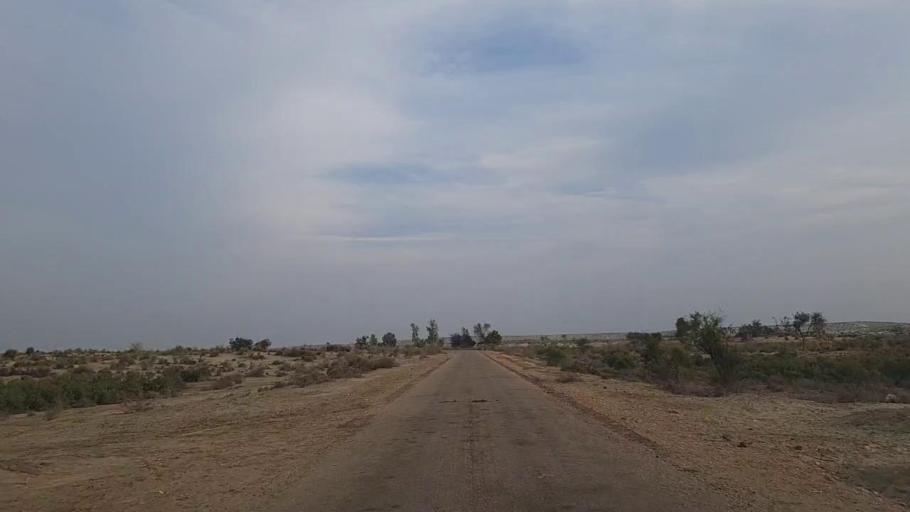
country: PK
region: Sindh
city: Daur
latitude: 26.4955
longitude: 68.5266
